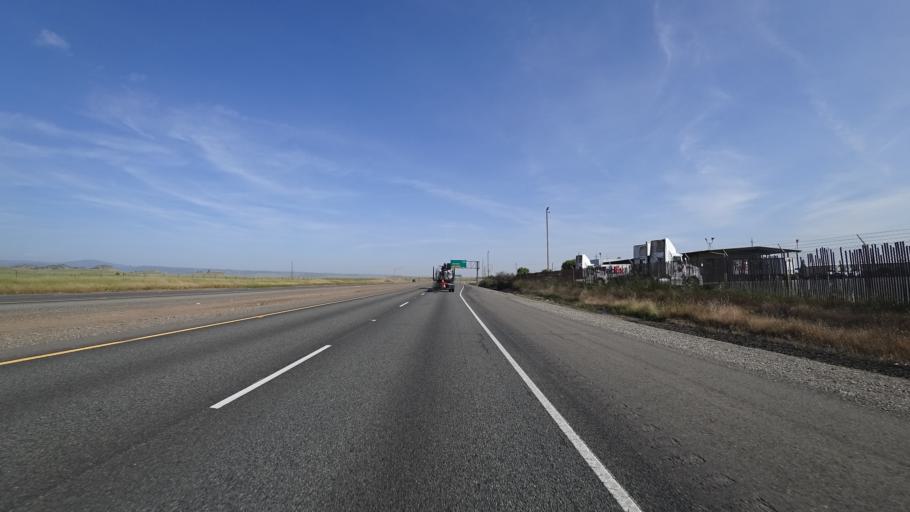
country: US
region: California
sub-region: Butte County
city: Durham
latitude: 39.6486
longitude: -121.7236
